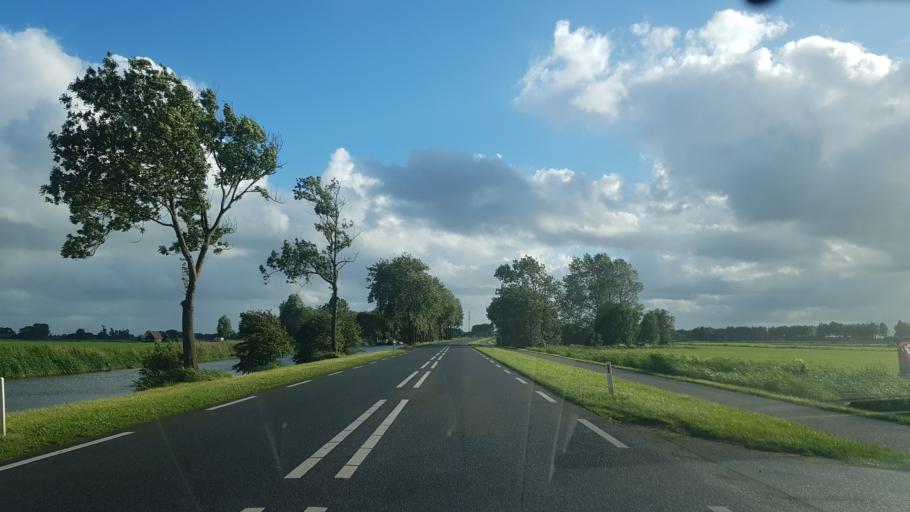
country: NL
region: Groningen
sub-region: Gemeente Slochteren
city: Slochteren
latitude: 53.2867
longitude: 6.7159
